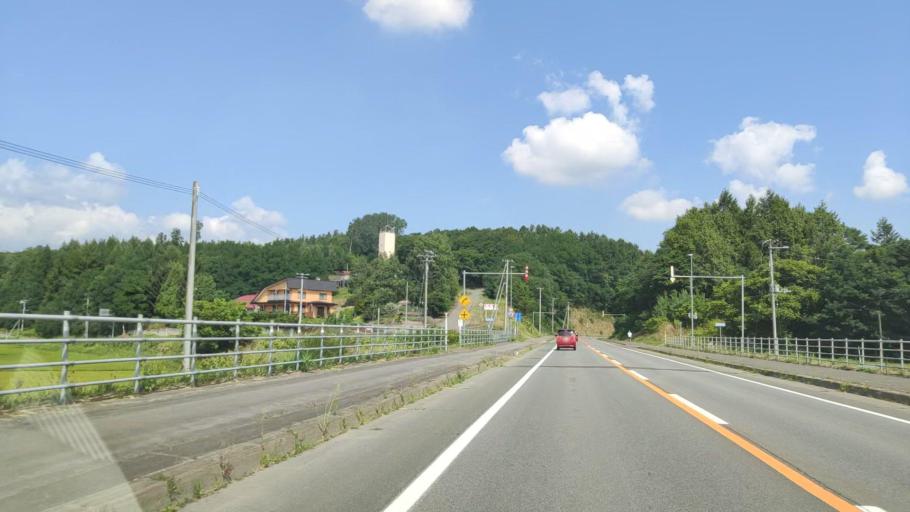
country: JP
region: Hokkaido
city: Shimo-furano
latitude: 43.4695
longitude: 142.4538
